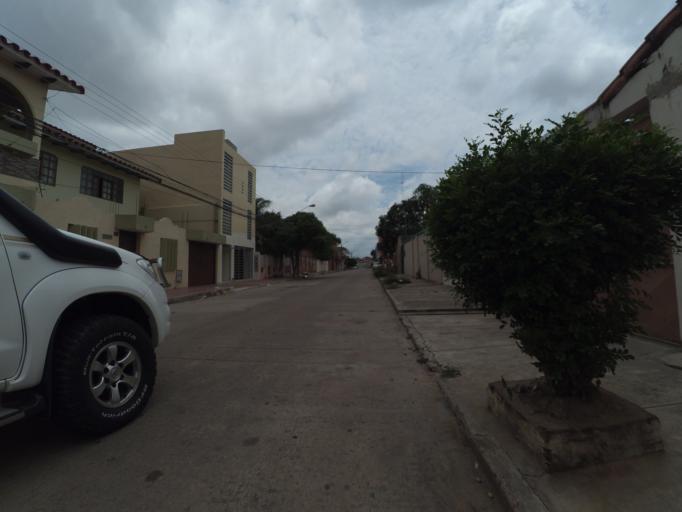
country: BO
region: Santa Cruz
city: Santa Cruz de la Sierra
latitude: -17.7899
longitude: -63.1972
